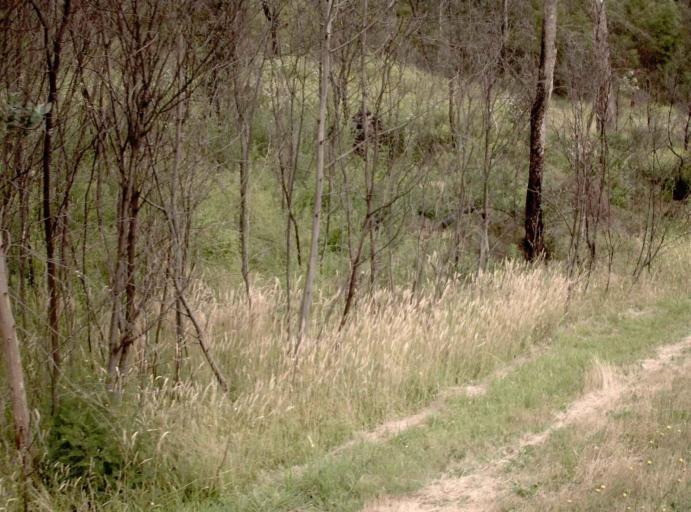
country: AU
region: Victoria
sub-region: Wellington
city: Heyfield
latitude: -37.7759
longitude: 146.6667
